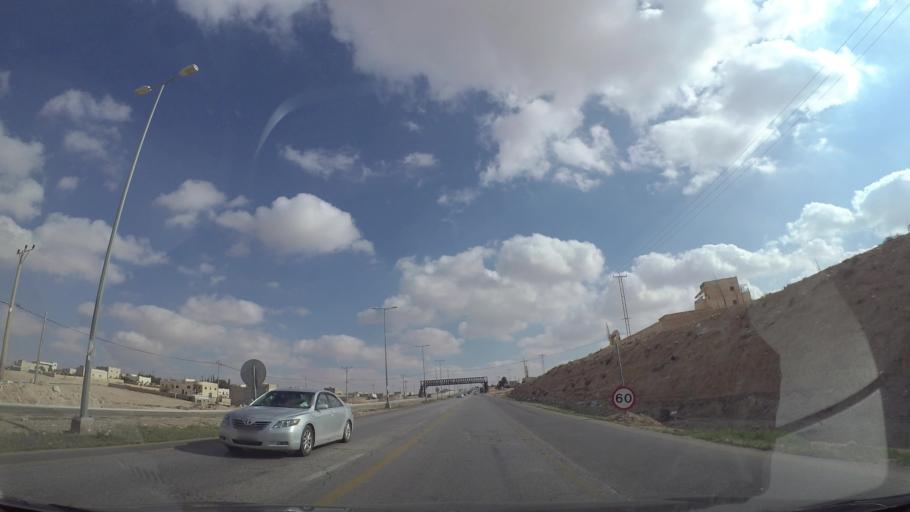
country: JO
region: Amman
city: Al Jizah
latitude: 31.6161
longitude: 35.9979
